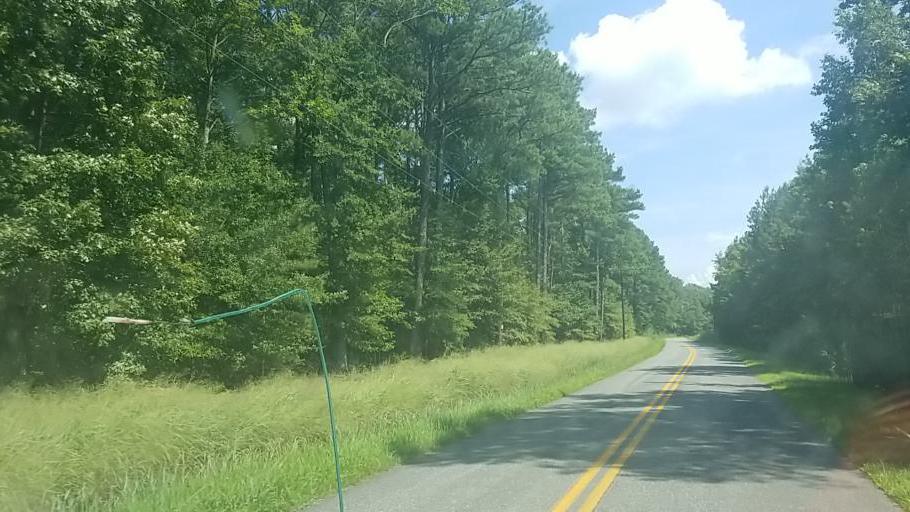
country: US
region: Maryland
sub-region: Dorchester County
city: Hurlock
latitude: 38.4331
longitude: -75.8895
